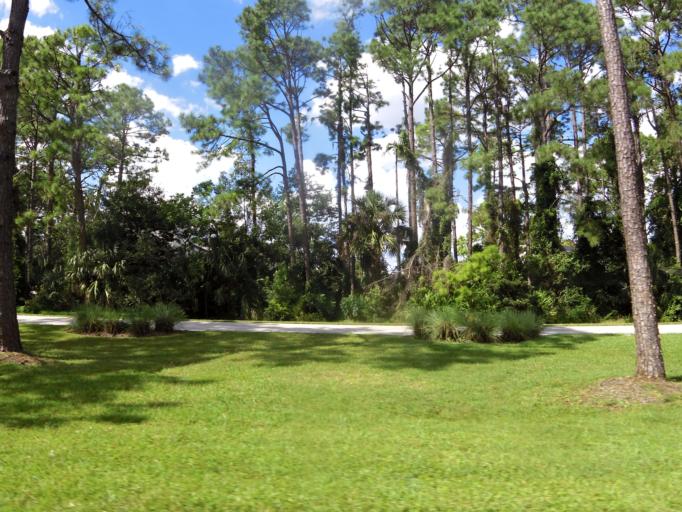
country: US
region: Florida
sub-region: Saint Johns County
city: Ponte Vedra Beach
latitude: 30.2491
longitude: -81.3918
